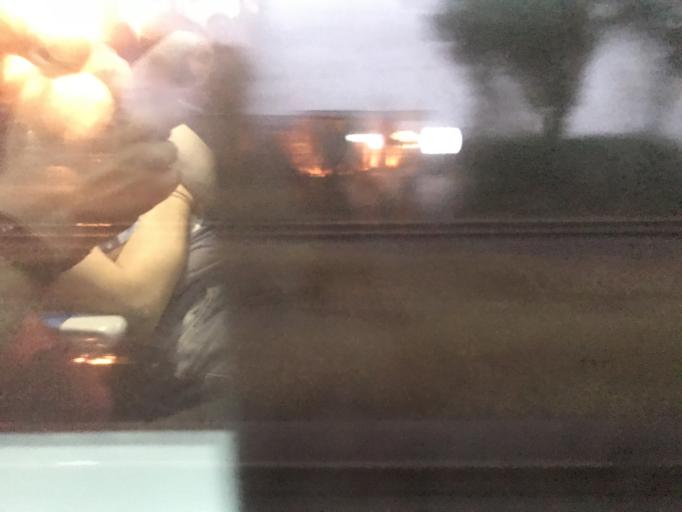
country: TR
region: Kocaeli
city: Korfez
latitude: 40.7727
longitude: 29.7321
